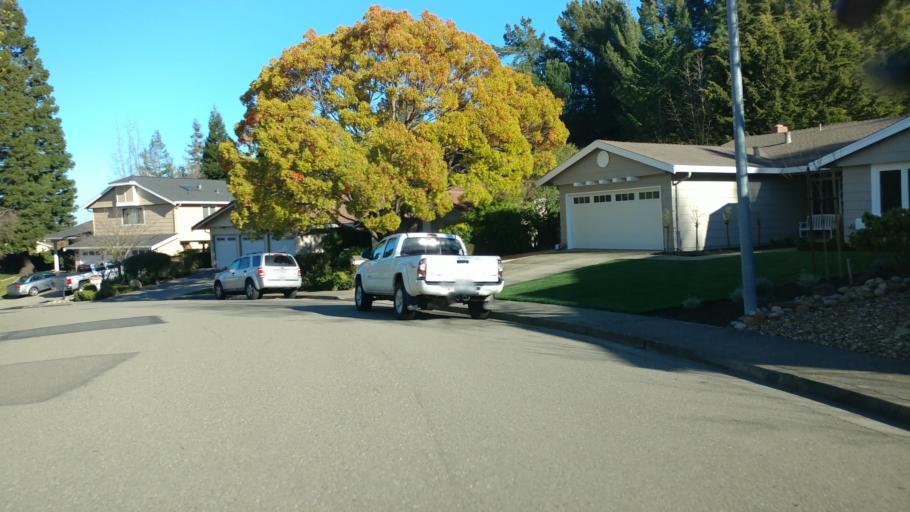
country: US
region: California
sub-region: Contra Costa County
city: San Ramon
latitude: 37.7600
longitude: -121.9816
